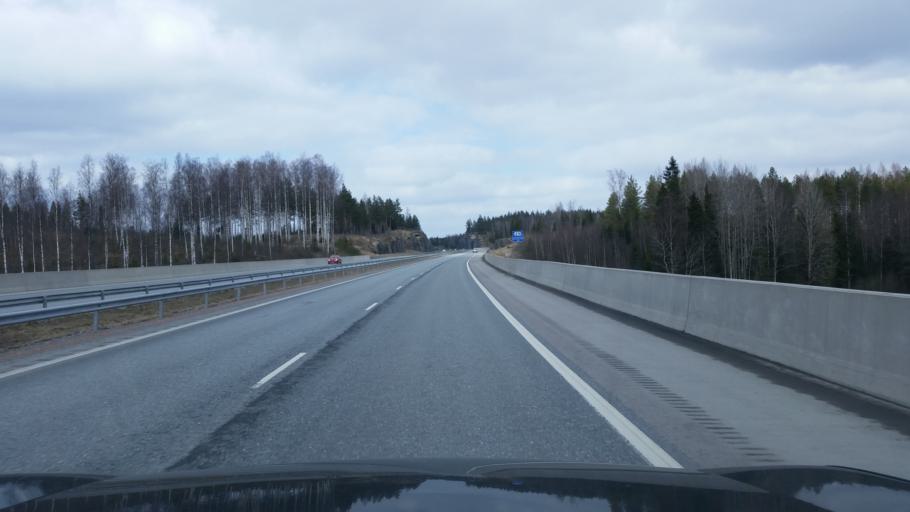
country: FI
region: Uusimaa
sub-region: Helsinki
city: Sammatti
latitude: 60.3531
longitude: 23.8942
